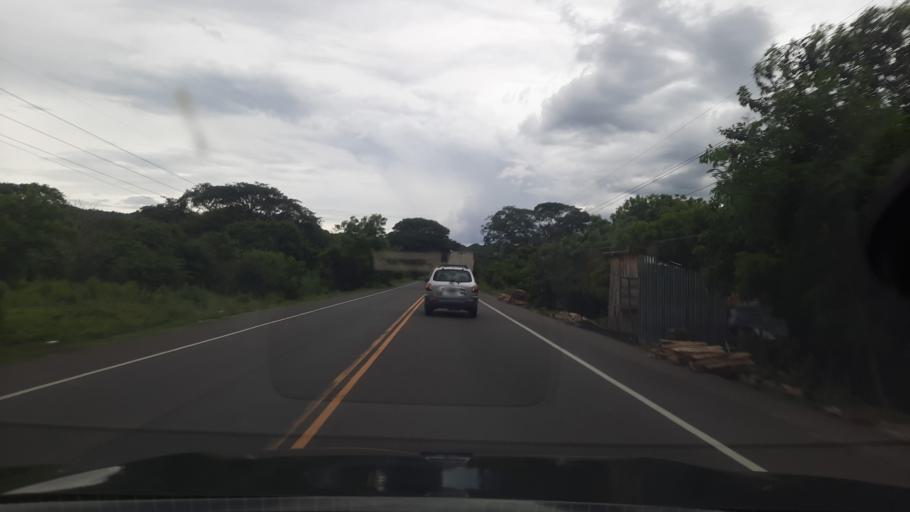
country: HN
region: Choluteca
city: Marcovia
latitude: 13.3717
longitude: -87.2975
